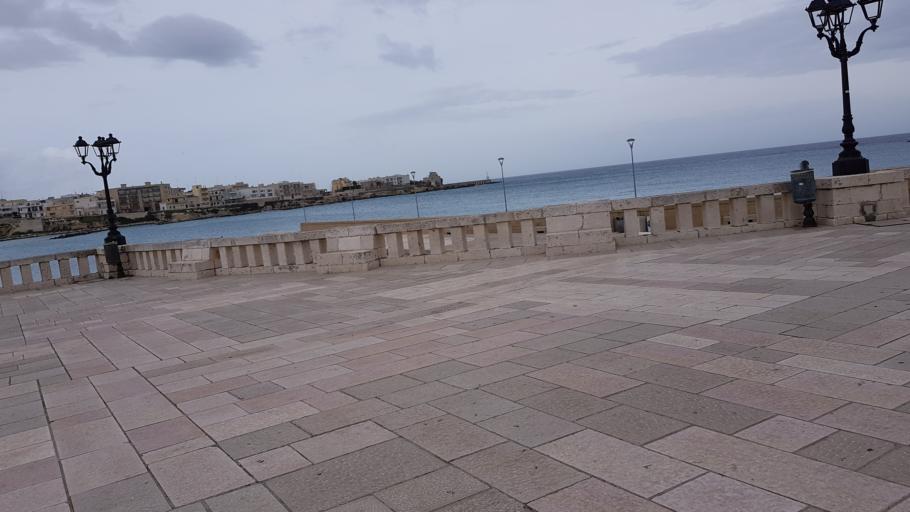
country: IT
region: Apulia
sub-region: Provincia di Lecce
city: Otranto
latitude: 40.1468
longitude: 18.4898
